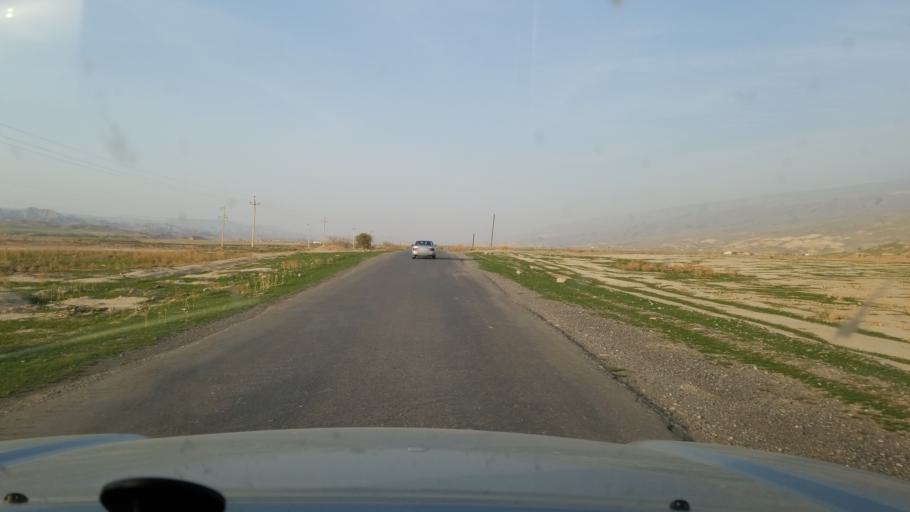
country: TM
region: Lebap
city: Gowurdak
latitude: 37.7486
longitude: 66.3499
